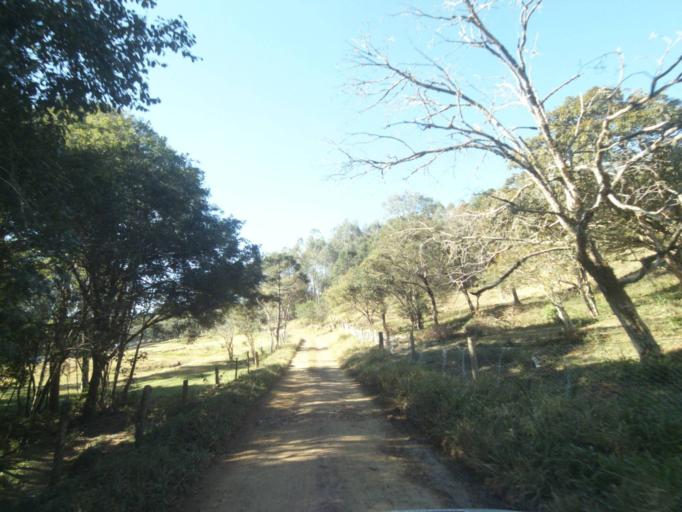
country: BR
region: Parana
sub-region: Tibagi
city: Tibagi
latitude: -24.5562
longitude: -50.5190
